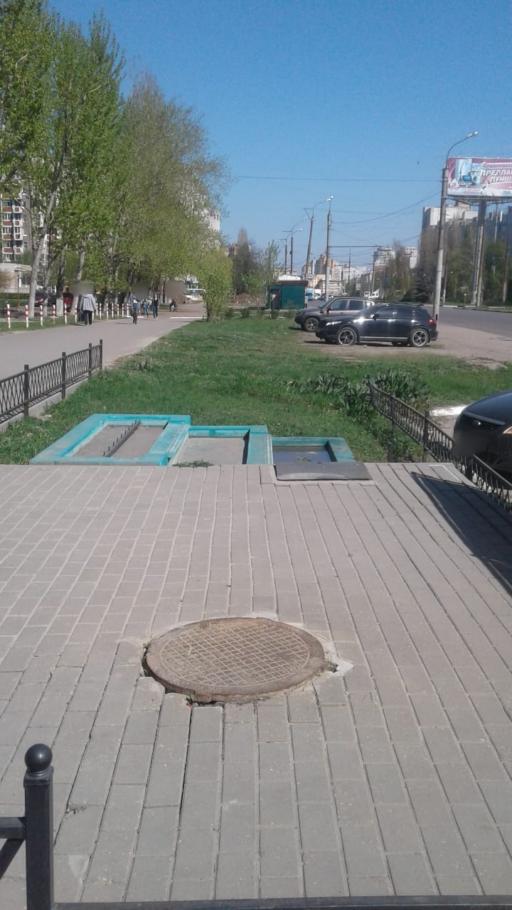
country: RU
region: Voronezj
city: Podgornoye
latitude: 51.7129
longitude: 39.1711
